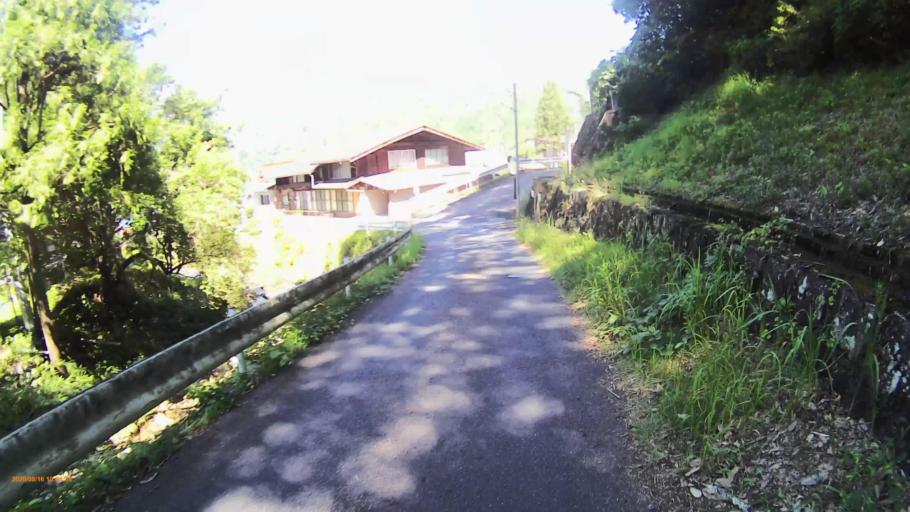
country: JP
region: Nagano
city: Iida
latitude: 35.6837
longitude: 137.6659
